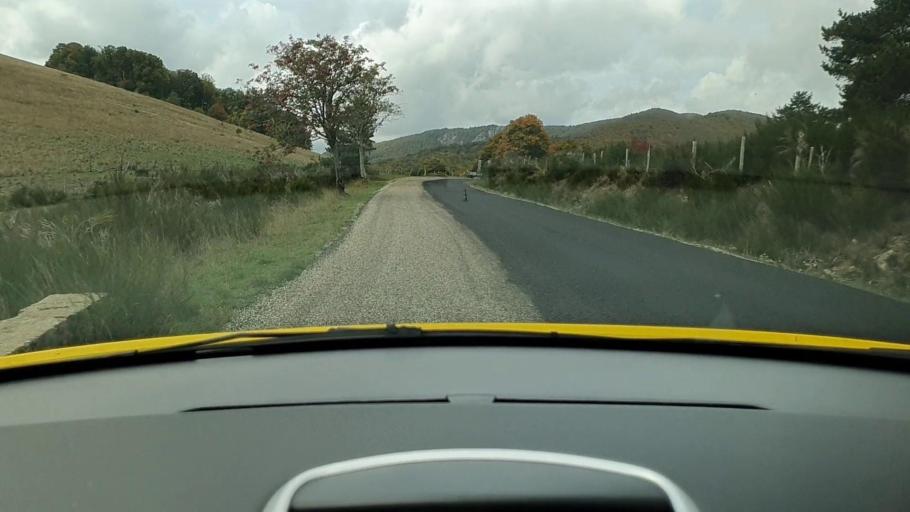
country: FR
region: Languedoc-Roussillon
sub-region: Departement du Gard
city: Valleraugue
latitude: 44.0731
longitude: 3.5353
